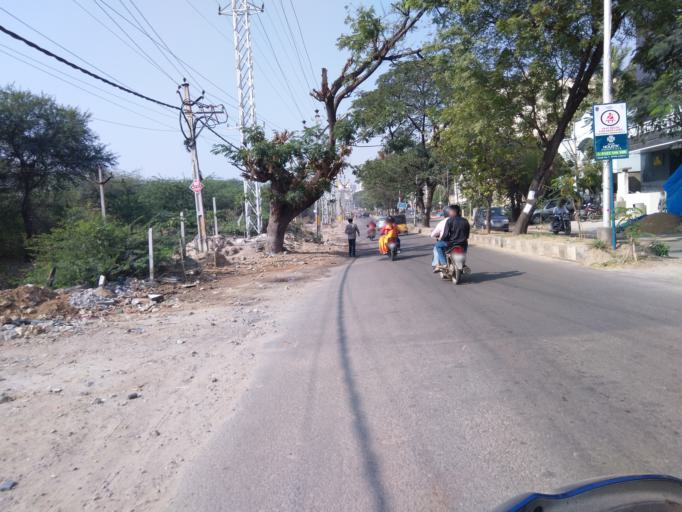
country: IN
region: Telangana
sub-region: Rangareddi
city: Kukatpalli
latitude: 17.4842
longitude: 78.3987
